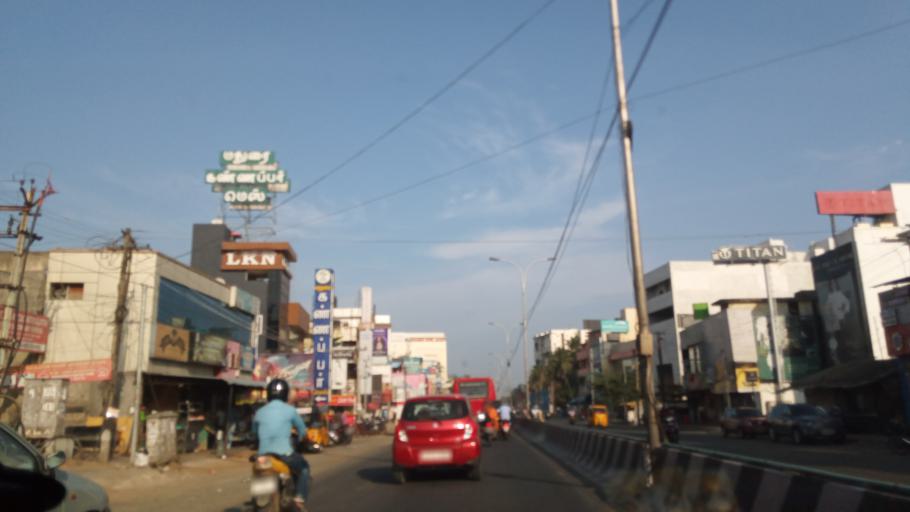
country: IN
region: Tamil Nadu
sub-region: Thiruvallur
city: Porur
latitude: 13.0338
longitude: 80.1608
